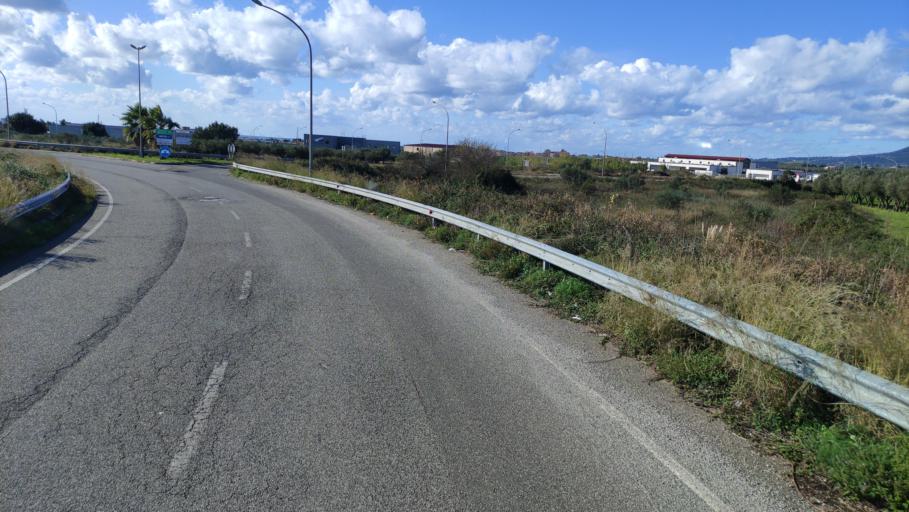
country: IT
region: Calabria
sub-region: Provincia di Catanzaro
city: Santa Eufemia Lamezia
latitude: 38.9209
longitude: 16.2732
